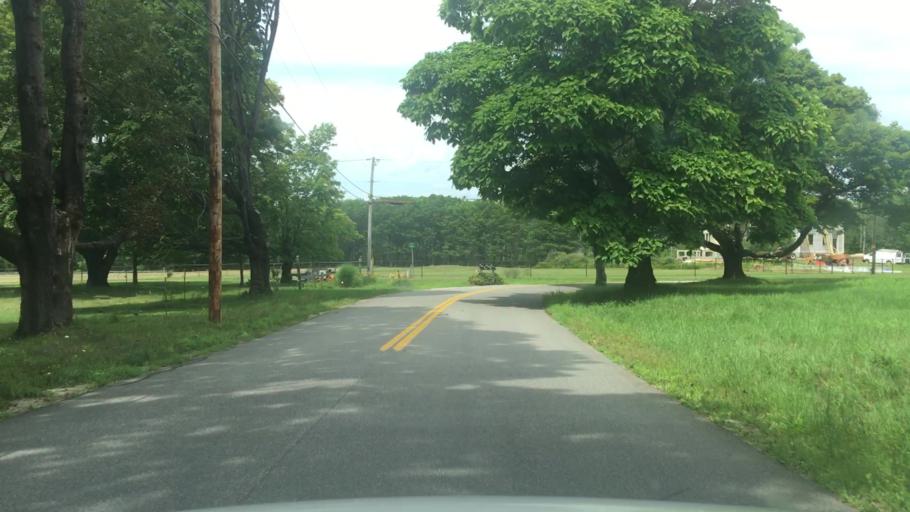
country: US
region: Maine
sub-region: Cumberland County
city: Scarborough
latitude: 43.5680
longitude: -70.2618
